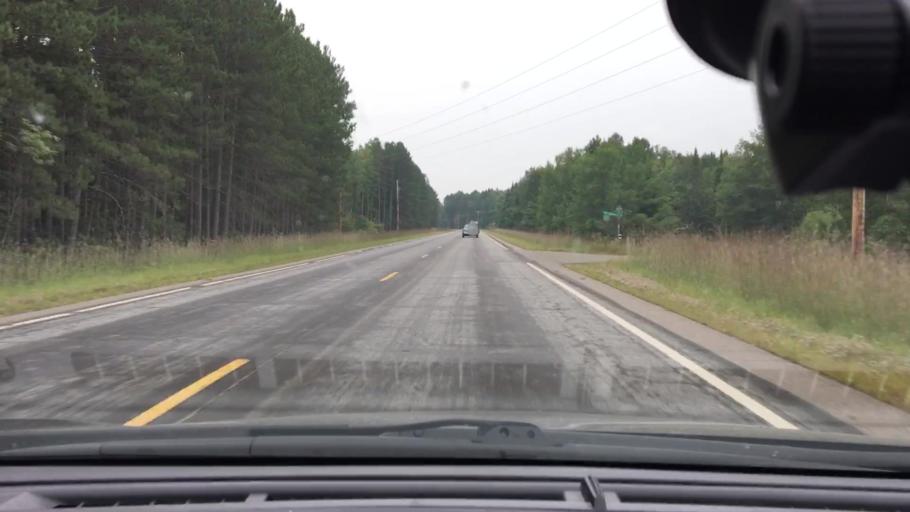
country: US
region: Minnesota
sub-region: Crow Wing County
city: Cross Lake
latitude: 46.8003
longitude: -93.9592
